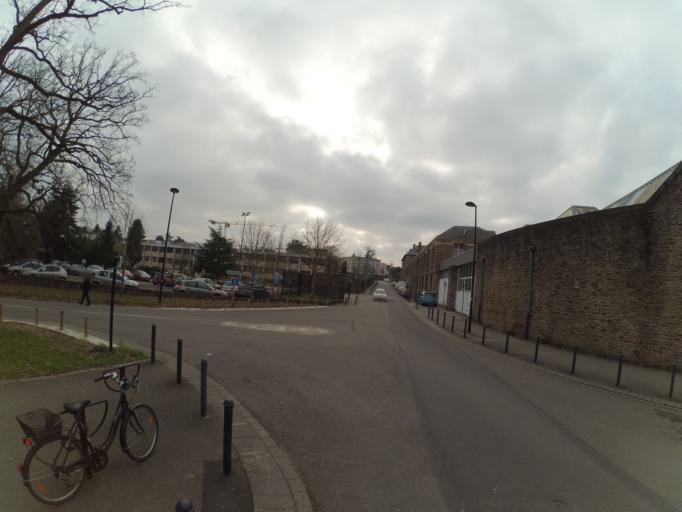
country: FR
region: Pays de la Loire
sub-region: Departement de la Loire-Atlantique
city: Nantes
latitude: 47.2396
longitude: -1.5551
